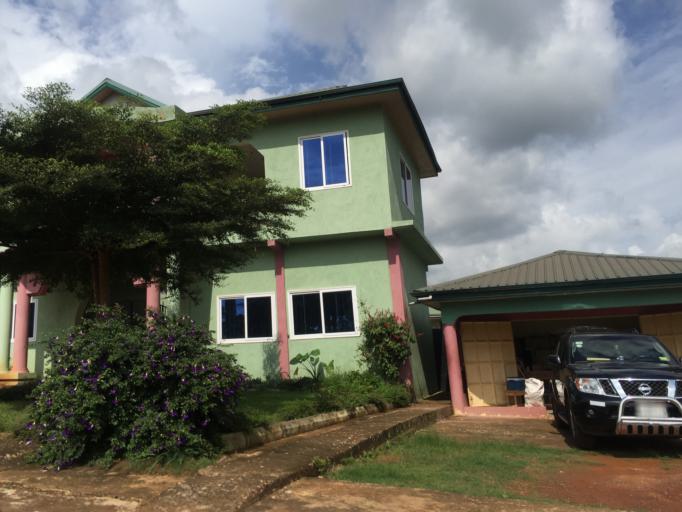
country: GH
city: Mpraeso
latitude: 6.6131
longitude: -0.7408
